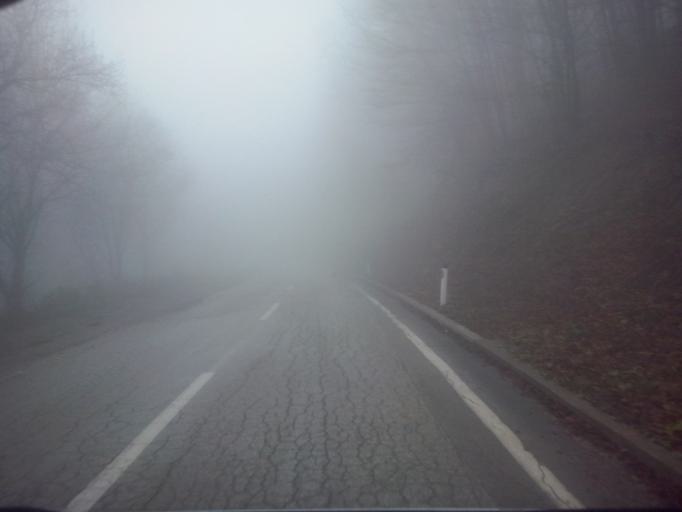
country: RS
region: Central Serbia
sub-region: Moravicki Okrug
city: Ivanjica
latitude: 43.5288
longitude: 20.3142
